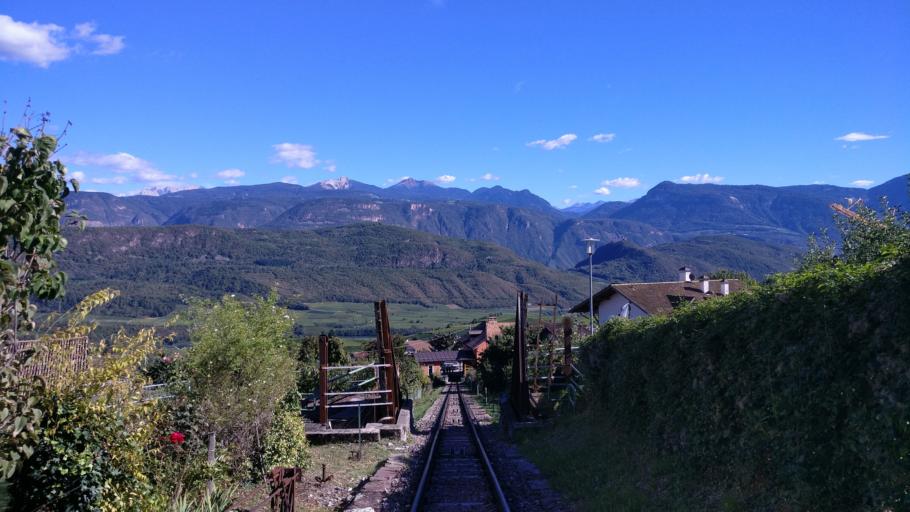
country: IT
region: Trentino-Alto Adige
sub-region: Bolzano
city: Caldaro sulla Strada del Vino
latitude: 46.4087
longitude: 11.2329
